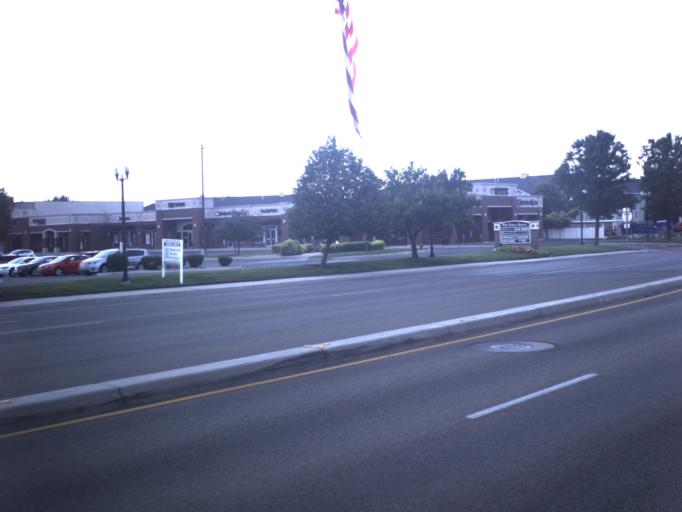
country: US
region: Utah
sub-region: Salt Lake County
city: Sandy City
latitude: 40.5888
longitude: -111.8907
